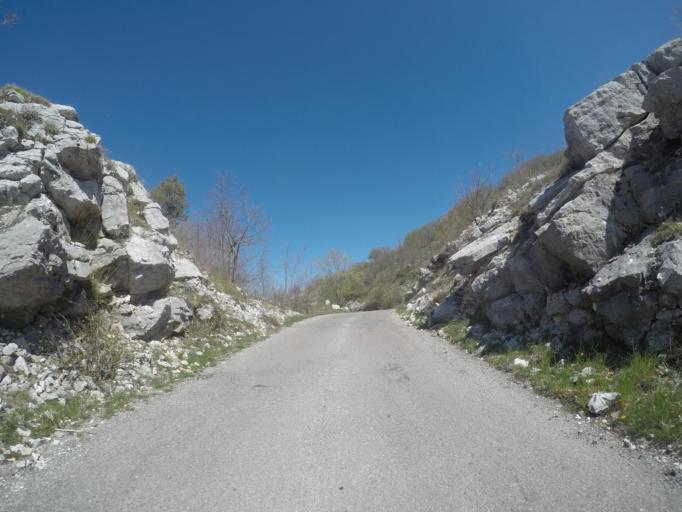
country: ME
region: Cetinje
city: Cetinje
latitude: 42.4429
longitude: 18.8741
